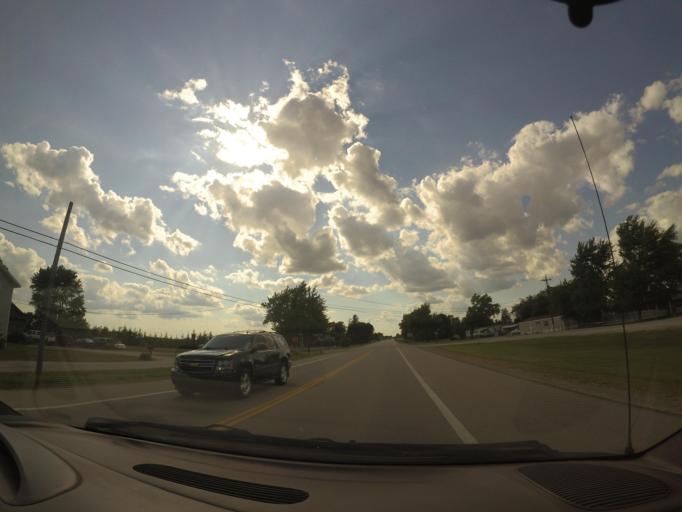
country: US
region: Ohio
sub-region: Wood County
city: Luckey
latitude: 41.4977
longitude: -83.4784
